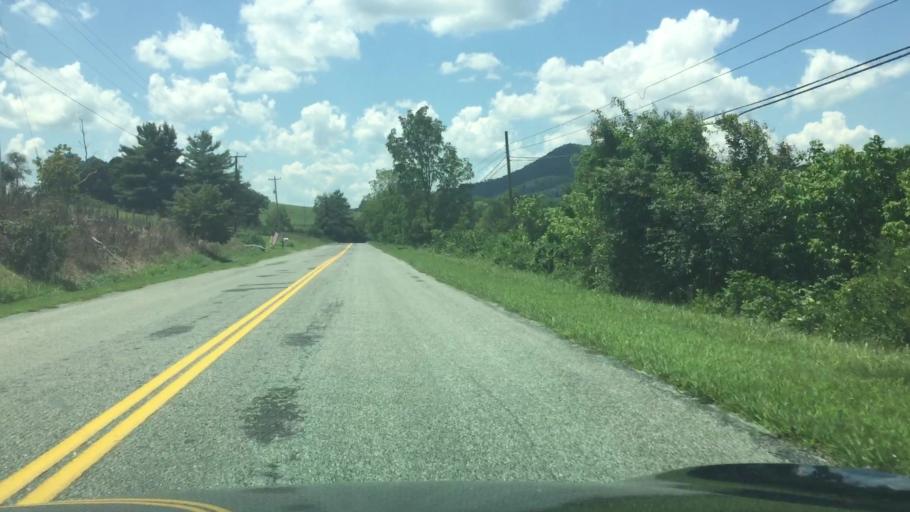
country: US
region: Virginia
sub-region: Pulaski County
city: Pulaski
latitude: 36.9795
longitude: -80.8306
